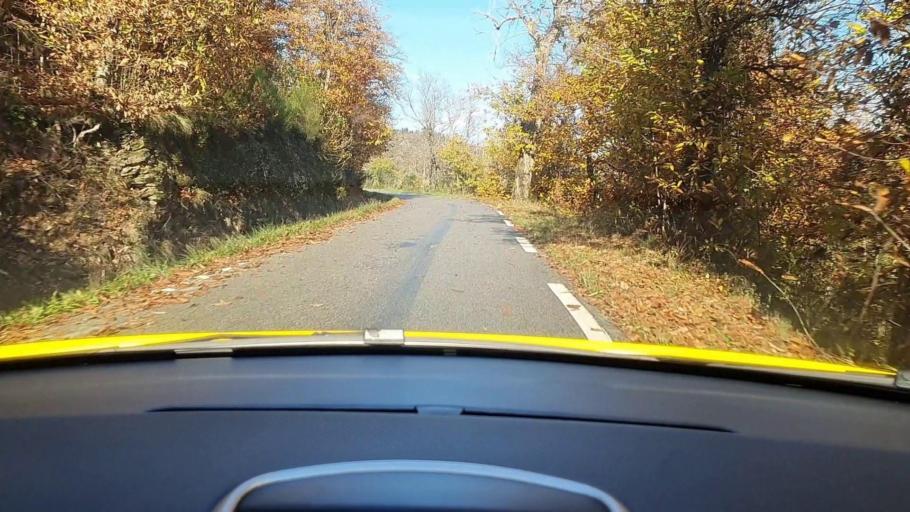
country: FR
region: Languedoc-Roussillon
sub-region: Departement du Gard
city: Valleraugue
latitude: 44.1635
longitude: 3.6374
